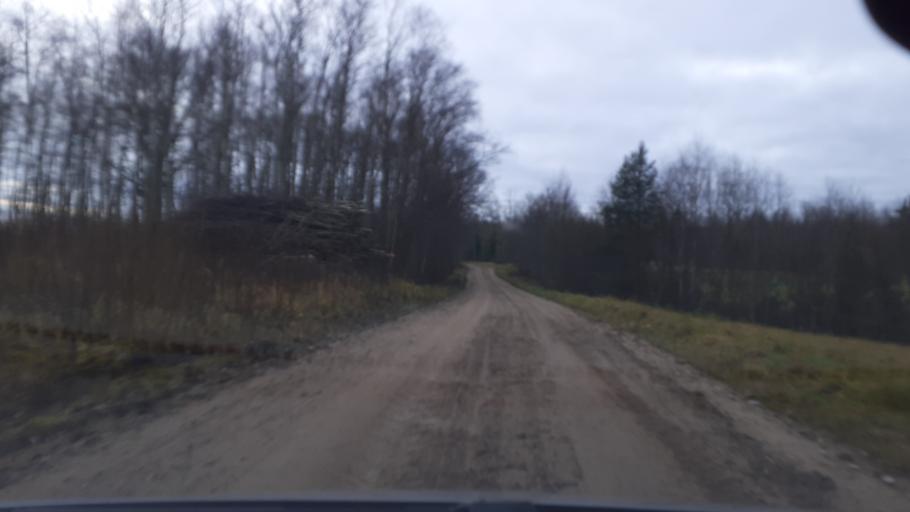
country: LV
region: Kuldigas Rajons
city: Kuldiga
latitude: 57.0033
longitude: 21.9213
